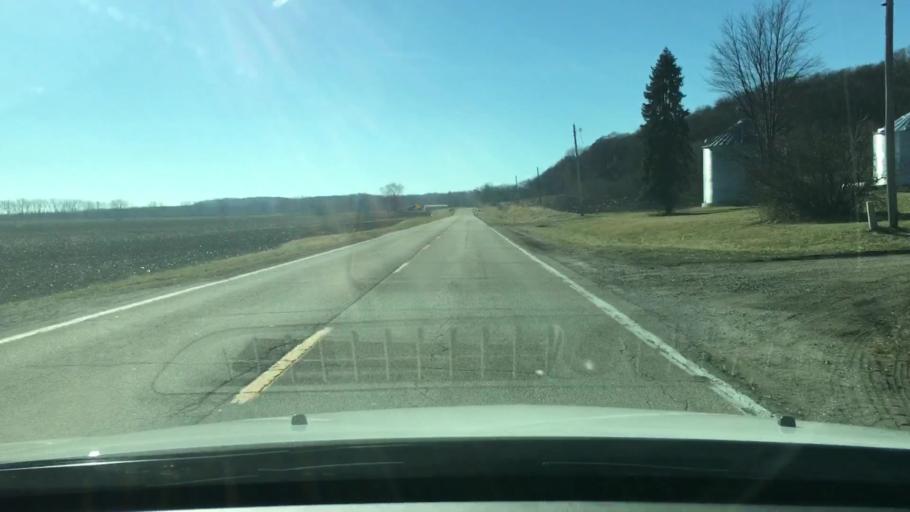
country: US
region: Illinois
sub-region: Mason County
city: Havana
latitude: 40.2387
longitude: -90.1933
